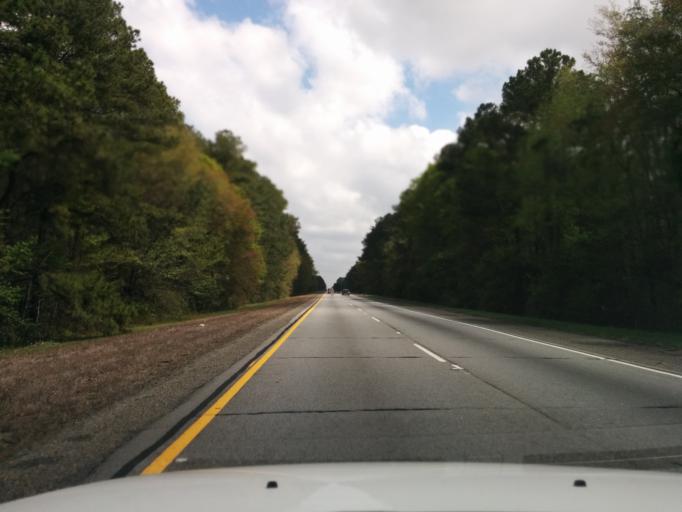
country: US
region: Georgia
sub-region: Bryan County
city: Pembroke
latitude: 32.2261
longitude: -81.5695
